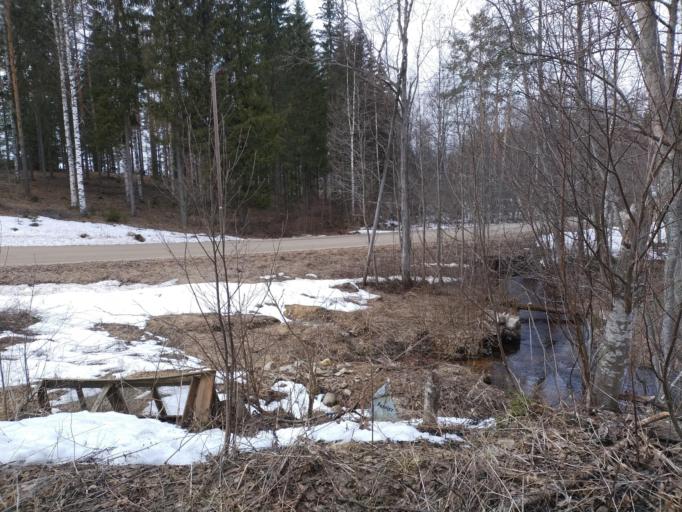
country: FI
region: Southern Savonia
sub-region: Savonlinna
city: Punkaharju
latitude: 61.6703
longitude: 29.2955
